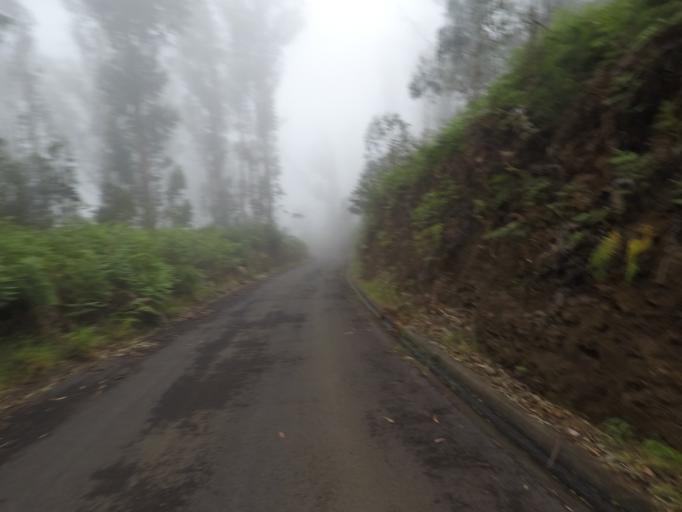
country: PT
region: Madeira
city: Ponta do Sol
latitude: 32.7118
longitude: -17.0949
